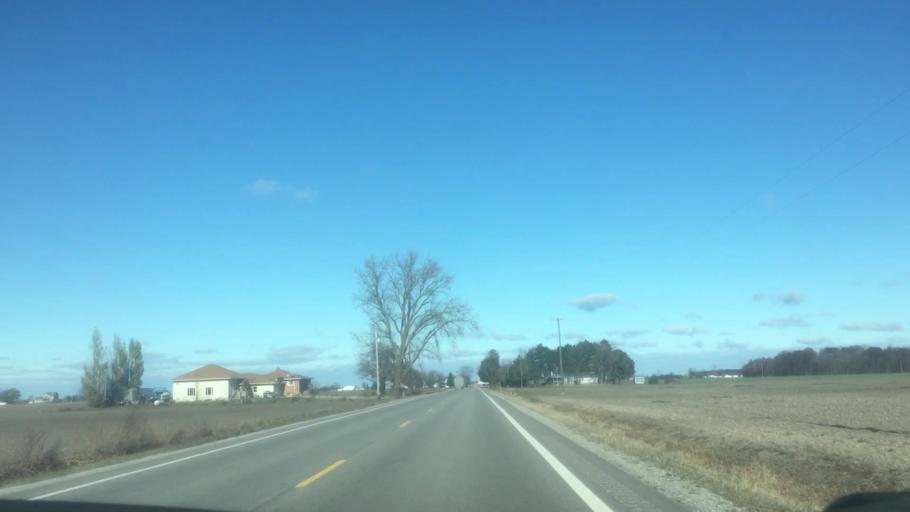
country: US
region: Michigan
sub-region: Bay County
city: Essexville
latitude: 43.5444
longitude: -83.7589
